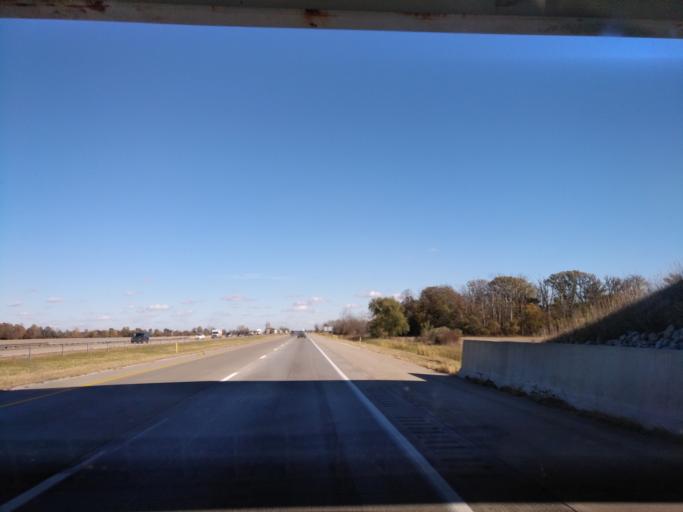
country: US
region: Indiana
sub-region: Marion County
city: Cumberland
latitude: 39.8195
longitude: -85.8782
